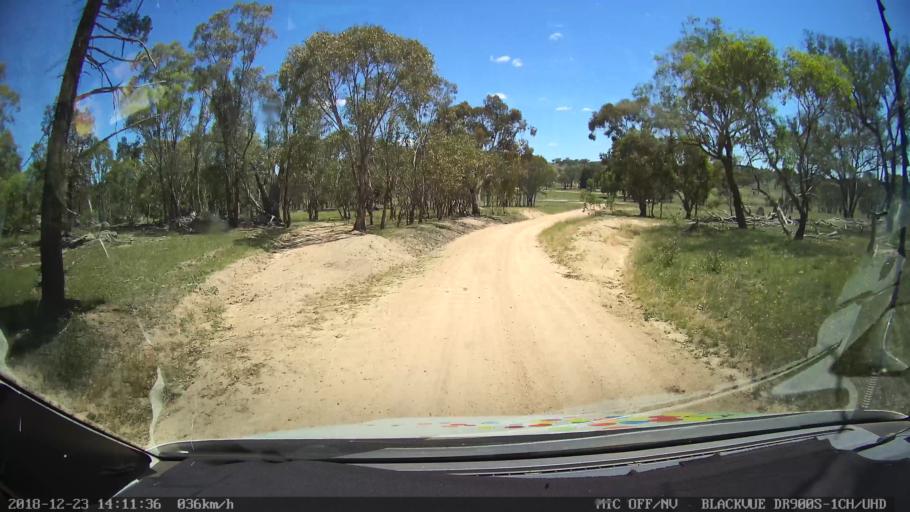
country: AU
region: New South Wales
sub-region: Tamworth Municipality
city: Manilla
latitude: -30.6520
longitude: 151.0497
